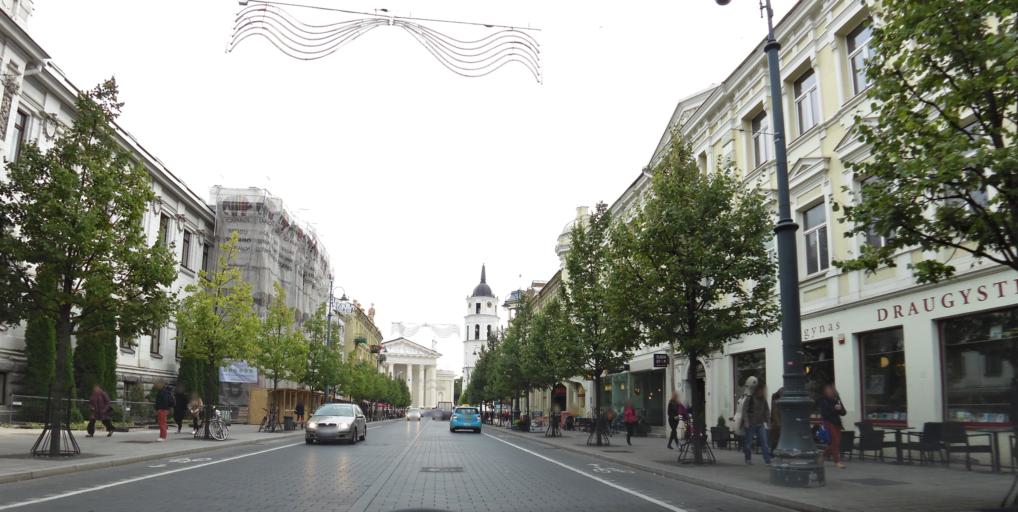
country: LT
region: Vilnius County
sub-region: Vilnius
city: Vilnius
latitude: 54.6864
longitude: 25.2841
